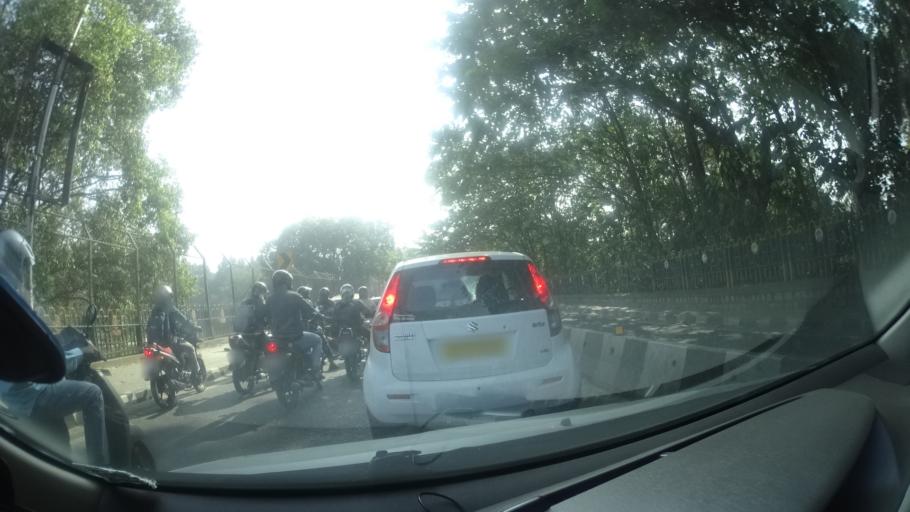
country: IN
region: Karnataka
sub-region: Bangalore Urban
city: Bangalore
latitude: 13.0077
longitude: 77.5764
